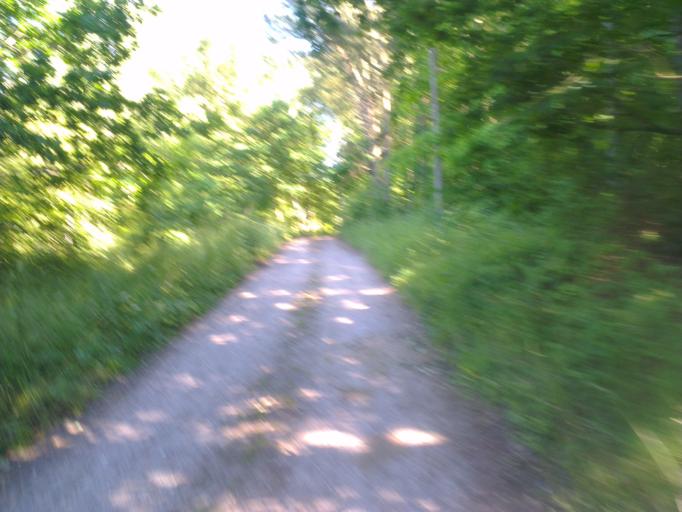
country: DK
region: Capital Region
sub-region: Frederikssund Kommune
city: Jaegerspris
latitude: 55.9088
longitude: 11.9166
